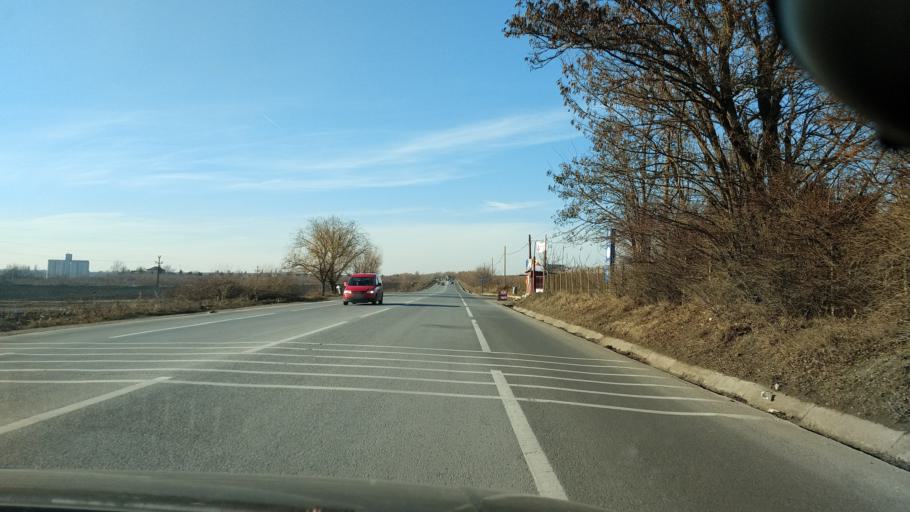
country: RO
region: Iasi
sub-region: Comuna Baltati
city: Baltati
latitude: 47.2226
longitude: 27.1708
